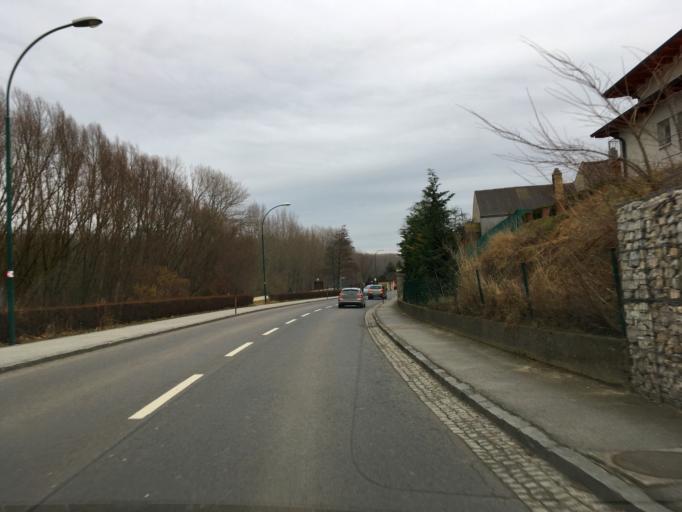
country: AT
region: Lower Austria
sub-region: Politischer Bezirk Bruck an der Leitha
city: Wolfsthal
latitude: 48.1338
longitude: 17.0149
